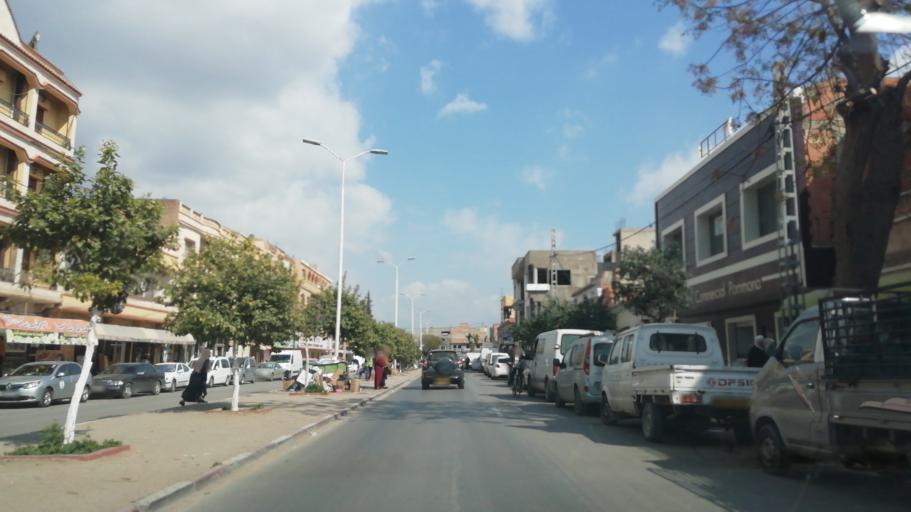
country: DZ
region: Mascara
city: Mascara
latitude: 35.5950
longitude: 0.0749
